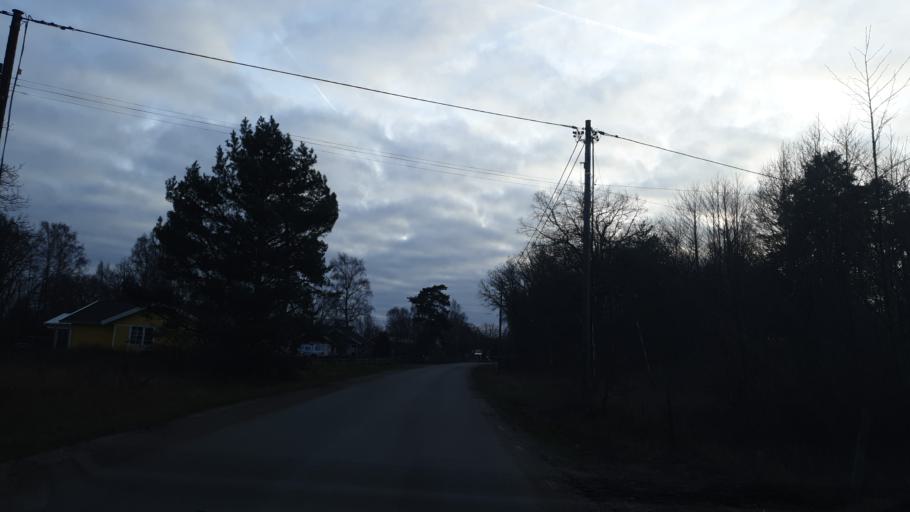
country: SE
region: Blekinge
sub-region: Karlskrona Kommun
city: Jaemjoe
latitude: 56.1541
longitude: 15.9053
